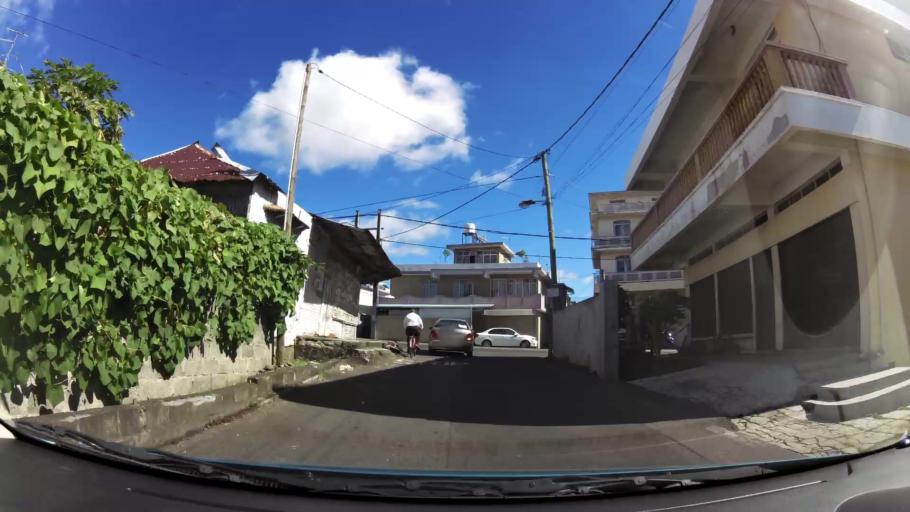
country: MU
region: Plaines Wilhems
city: Vacoas
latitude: -20.2963
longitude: 57.4838
